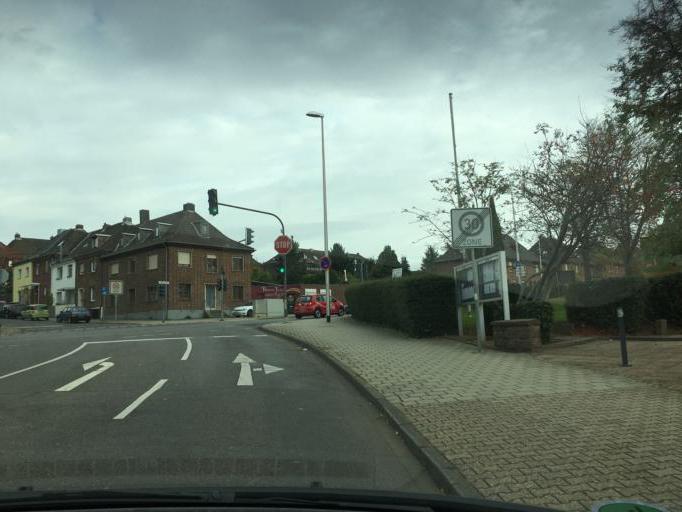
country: DE
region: North Rhine-Westphalia
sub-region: Regierungsbezirk Koln
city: Dueren
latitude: 50.7928
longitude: 6.4948
